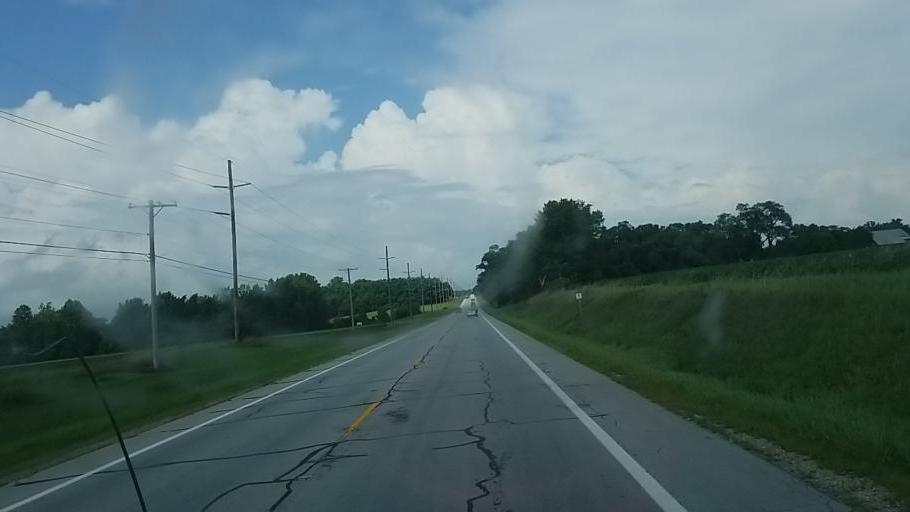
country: US
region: Ohio
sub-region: Champaign County
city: Urbana
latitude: 40.1417
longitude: -83.7469
